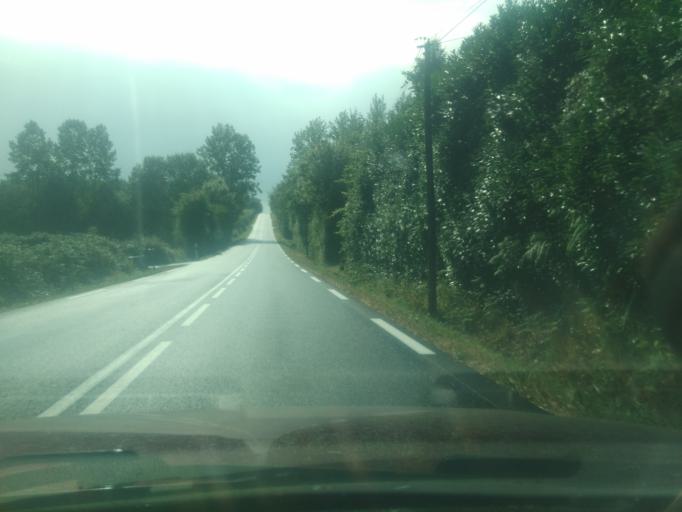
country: FR
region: Poitou-Charentes
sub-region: Departement des Deux-Sevres
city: Secondigny
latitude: 46.6126
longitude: -0.4361
